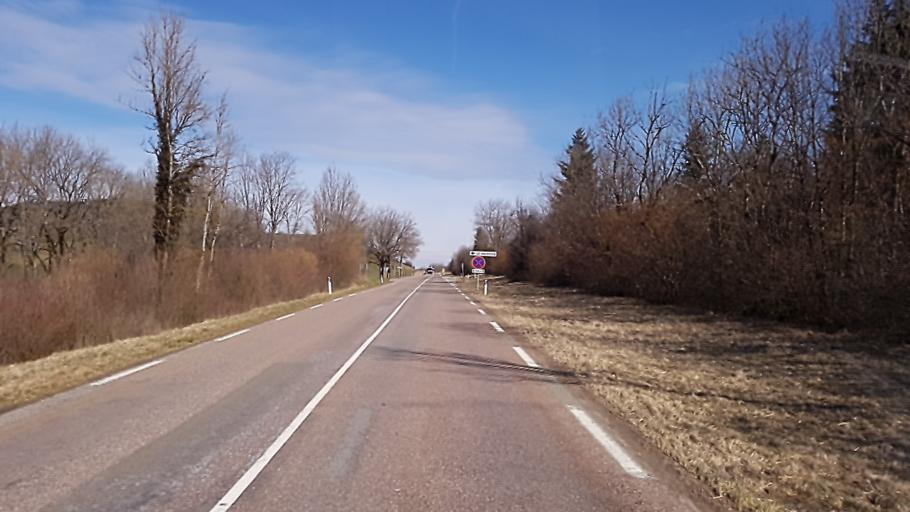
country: FR
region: Franche-Comte
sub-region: Departement du Jura
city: Champagnole
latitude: 46.6909
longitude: 5.9303
